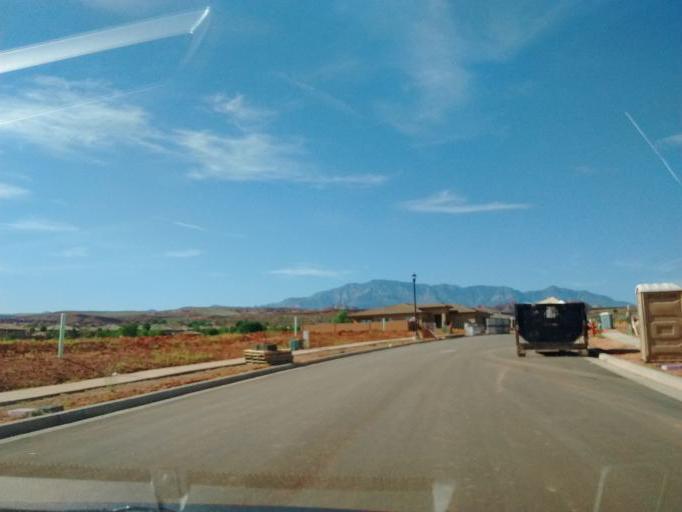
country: US
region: Utah
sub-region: Washington County
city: Washington
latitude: 37.1359
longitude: -113.4813
